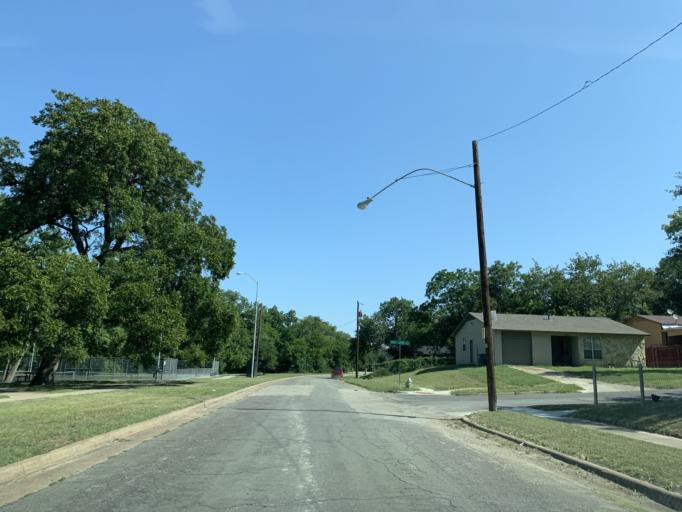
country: US
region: Texas
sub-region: Dallas County
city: Hutchins
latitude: 32.6691
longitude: -96.7489
